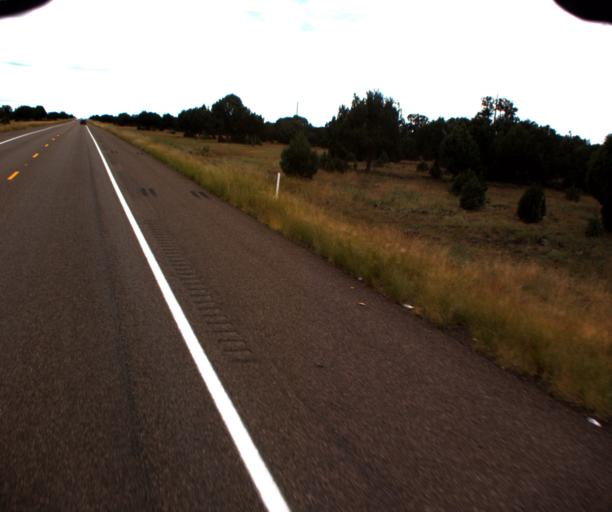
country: US
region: Arizona
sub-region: Navajo County
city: White Mountain Lake
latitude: 34.3209
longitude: -110.0431
